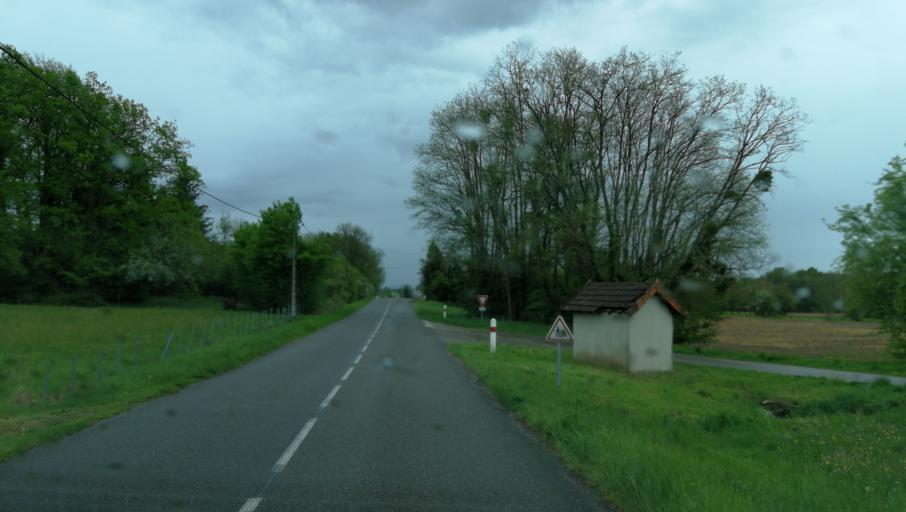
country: FR
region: Franche-Comte
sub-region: Departement du Jura
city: Bletterans
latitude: 46.7862
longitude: 5.4143
